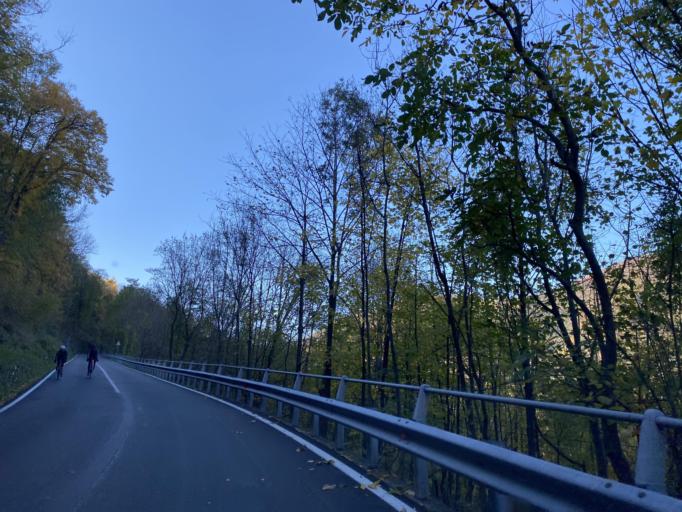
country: IT
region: Lombardy
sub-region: Provincia di Como
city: Laino
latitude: 45.9886
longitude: 9.0780
